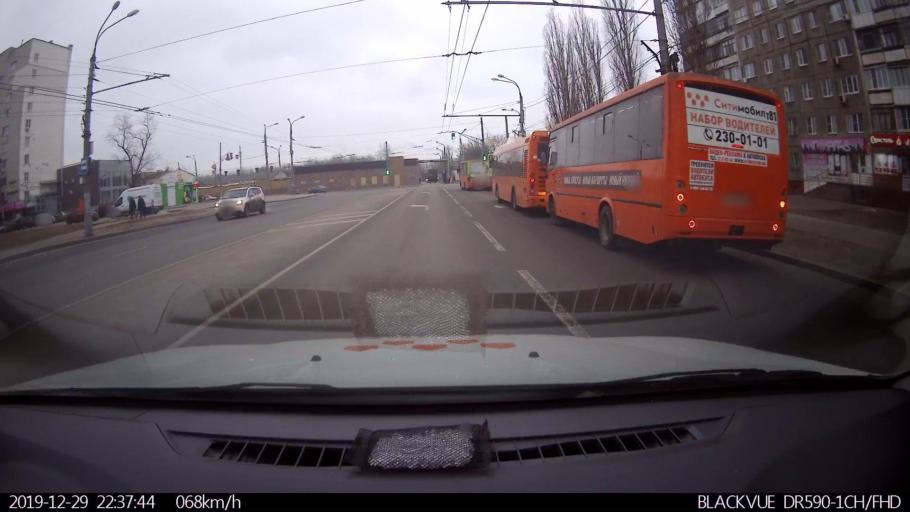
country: RU
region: Nizjnij Novgorod
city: Nizhniy Novgorod
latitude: 56.2624
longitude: 43.8972
